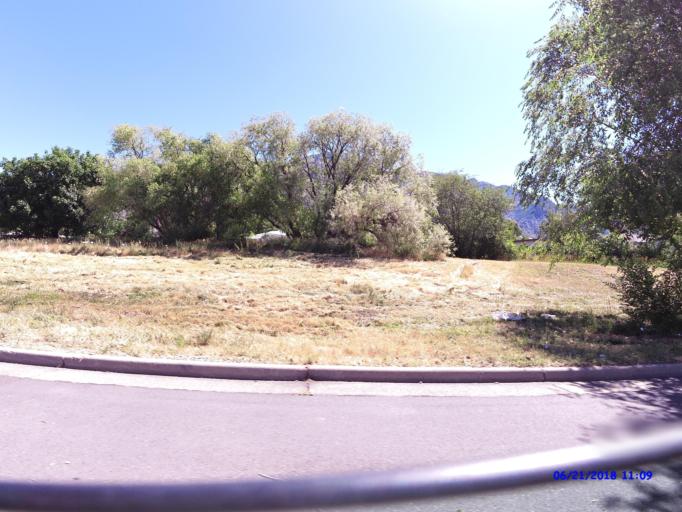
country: US
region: Utah
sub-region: Weber County
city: Harrisville
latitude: 41.2606
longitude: -111.9569
